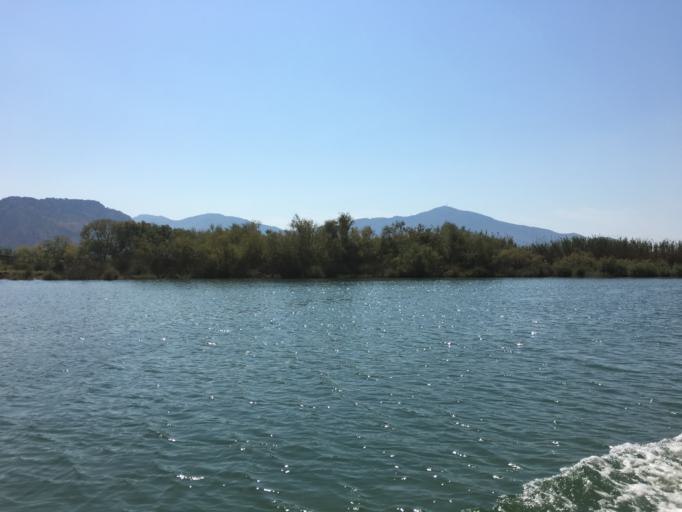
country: TR
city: Dalyan
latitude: 36.8187
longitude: 28.6361
